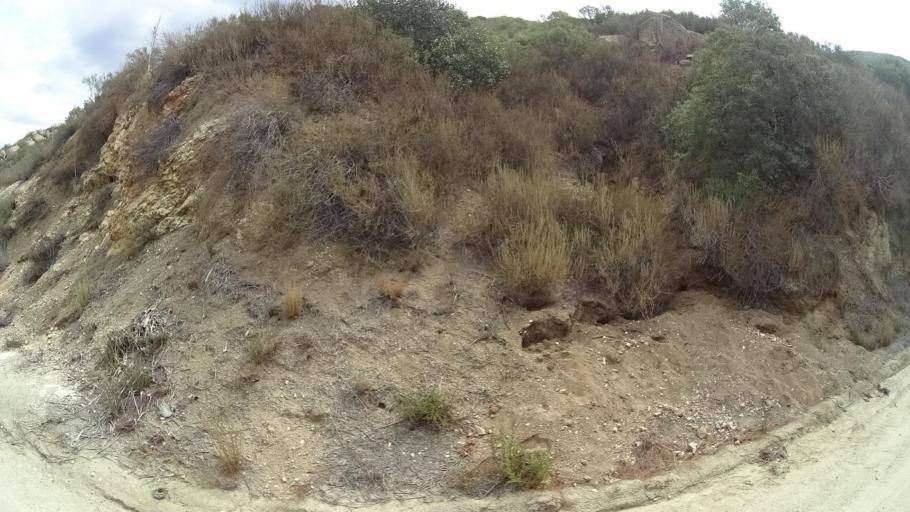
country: US
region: California
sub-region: San Diego County
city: Ramona
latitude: 33.1211
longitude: -116.8064
